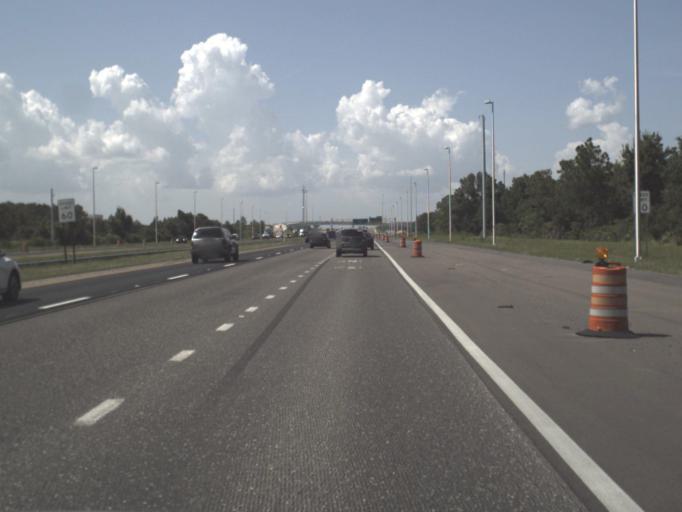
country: US
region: Florida
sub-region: Hillsborough County
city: Pebble Creek
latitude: 28.1107
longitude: -82.3700
